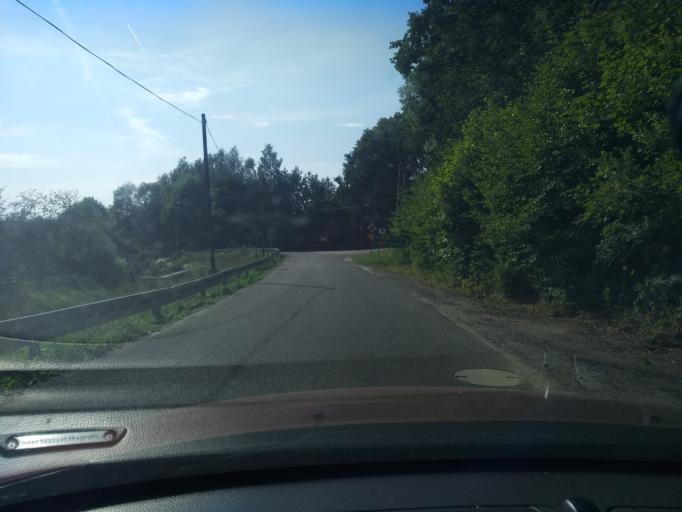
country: PL
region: Lower Silesian Voivodeship
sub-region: Powiat lubanski
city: Siekierczyn
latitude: 51.0866
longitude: 15.1404
